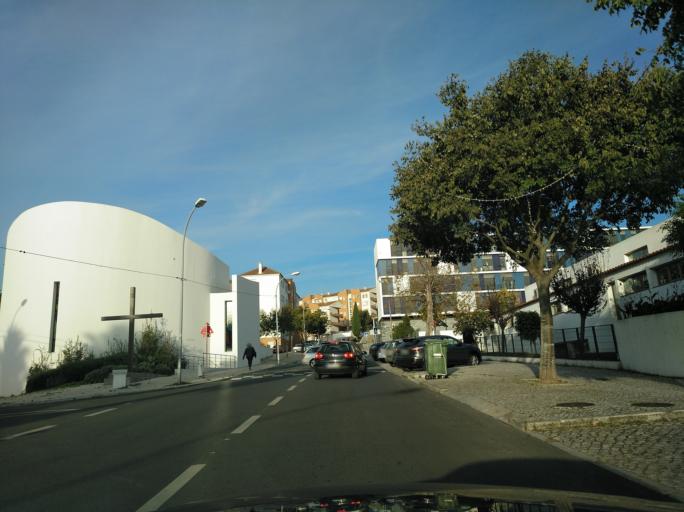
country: PT
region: Lisbon
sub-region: Oeiras
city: Linda-a-Velha
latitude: 38.7238
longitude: -9.2246
